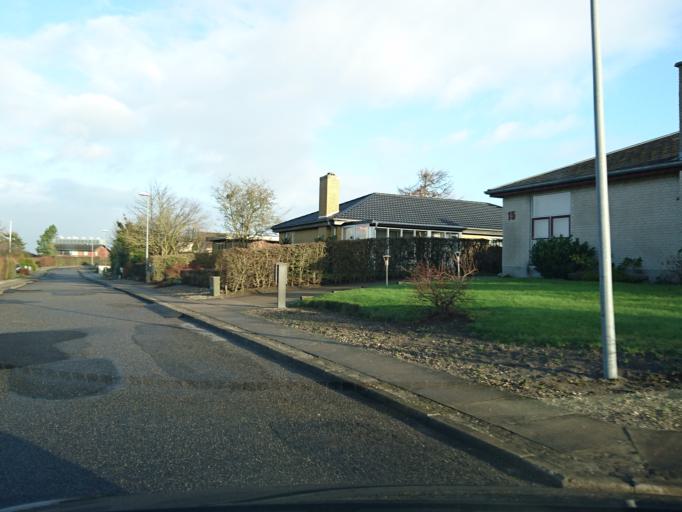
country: DK
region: North Denmark
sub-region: Alborg Kommune
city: Aalborg
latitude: 57.0152
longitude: 9.9361
